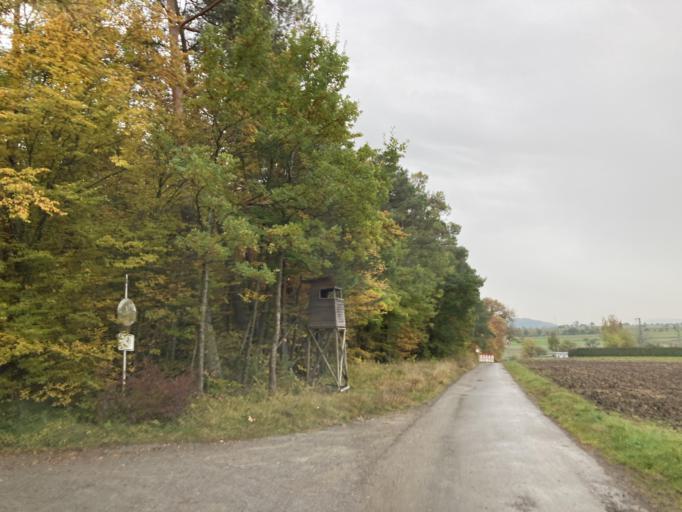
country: DE
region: Baden-Wuerttemberg
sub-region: Regierungsbezirk Stuttgart
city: Hildrizhausen
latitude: 48.5623
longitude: 8.9329
